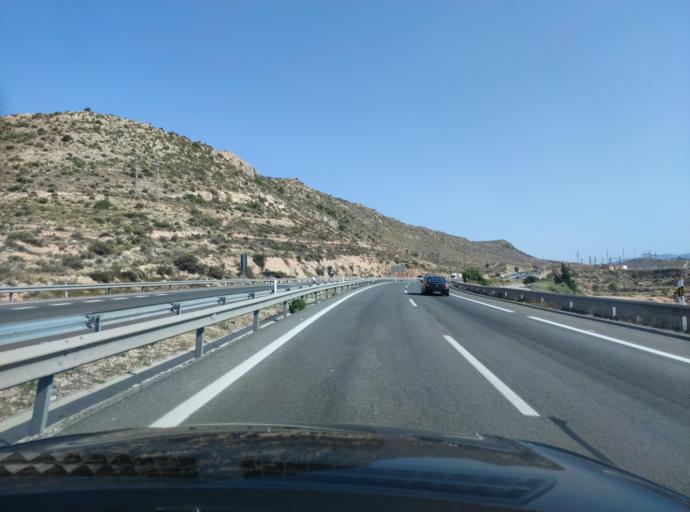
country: ES
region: Valencia
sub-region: Provincia de Alicante
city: Elda
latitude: 38.4337
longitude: -0.7829
